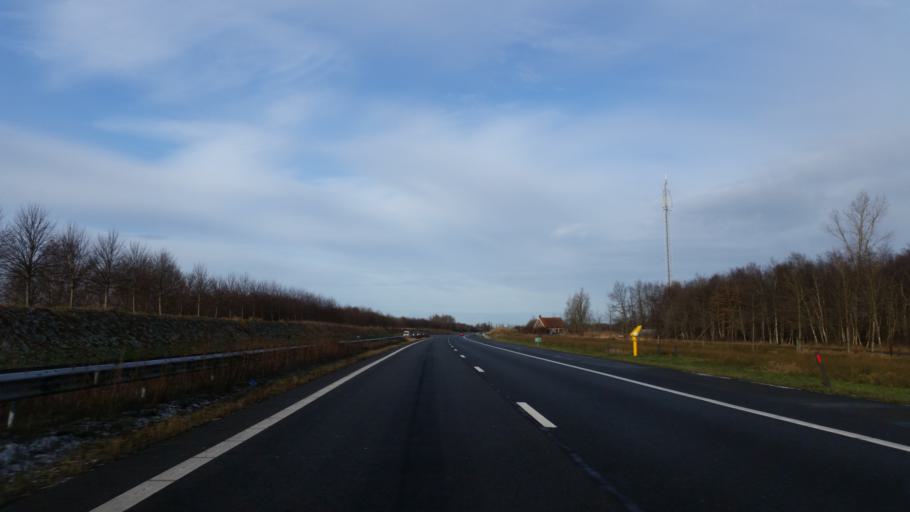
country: NL
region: Friesland
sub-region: Gemeente Skarsterlan
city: Oudehaske
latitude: 52.9921
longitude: 5.8860
